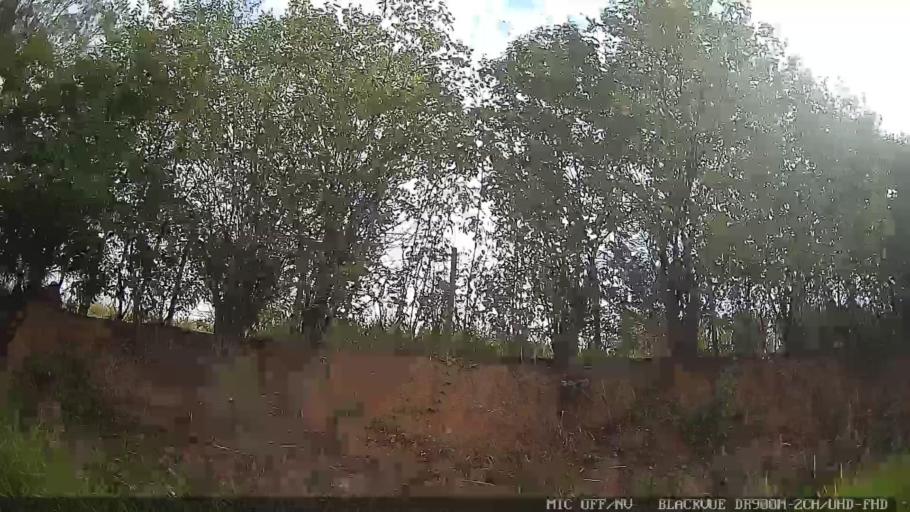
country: BR
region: Sao Paulo
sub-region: Salto
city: Salto
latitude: -23.1671
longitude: -47.2688
